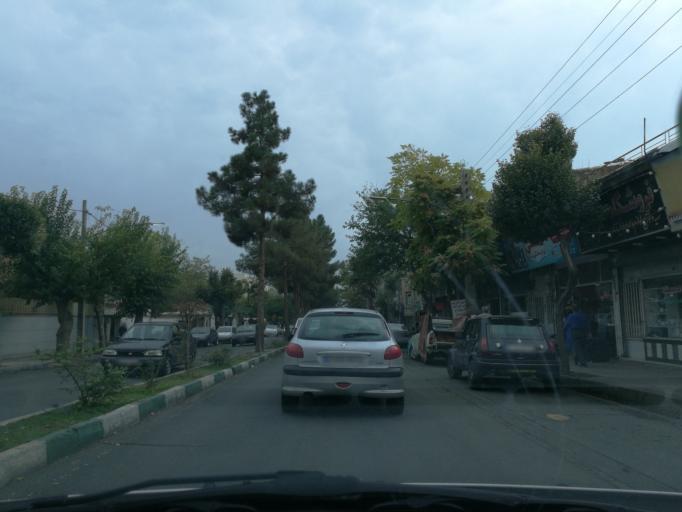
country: IR
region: Alborz
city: Karaj
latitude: 35.8481
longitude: 50.9687
